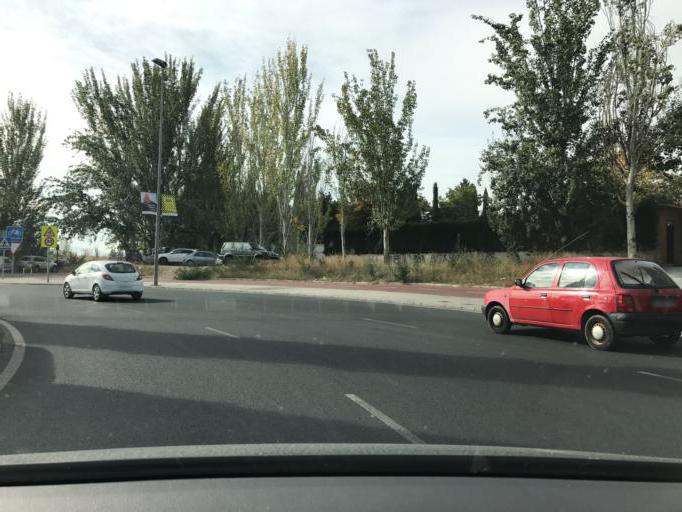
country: ES
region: Andalusia
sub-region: Provincia de Granada
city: Granada
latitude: 37.1678
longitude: -3.6105
